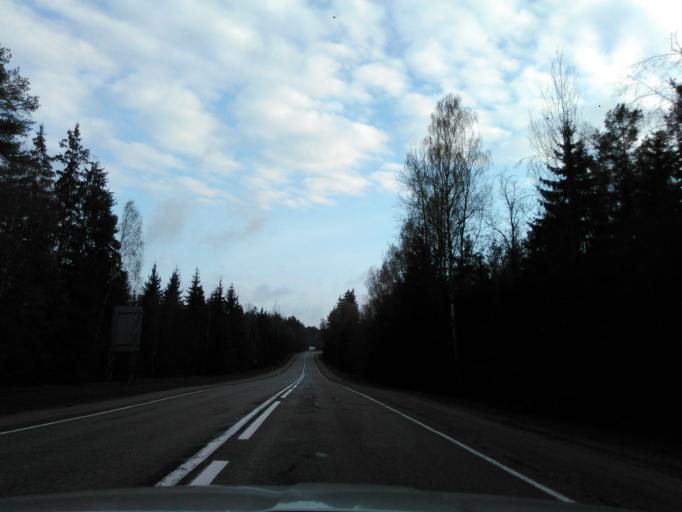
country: BY
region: Minsk
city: Lahoysk
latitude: 54.2783
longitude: 27.8626
